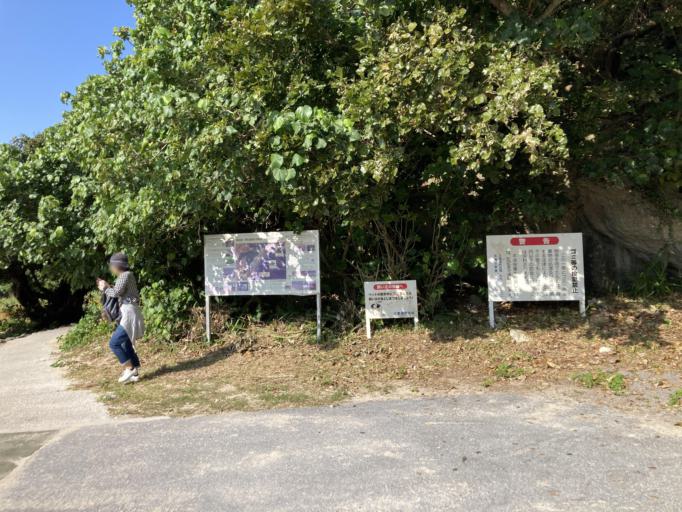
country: JP
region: Okinawa
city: Itoman
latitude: 26.1193
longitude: 127.7478
